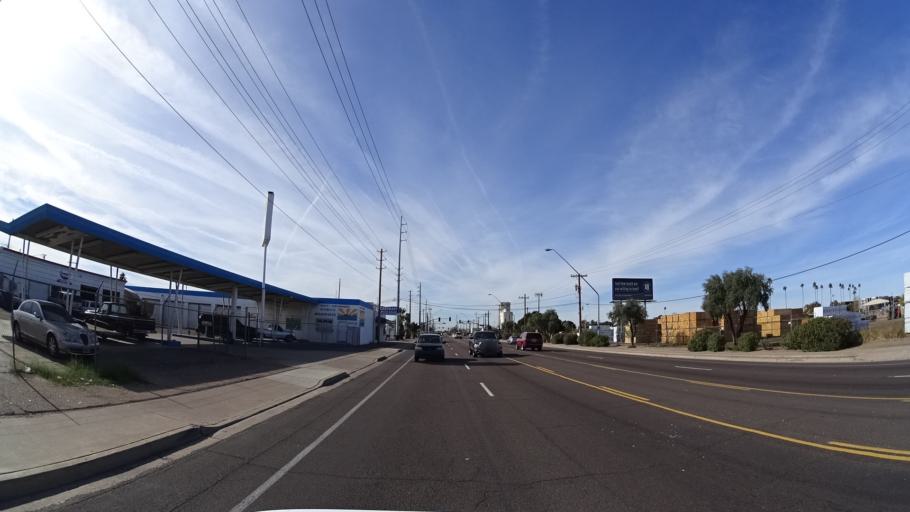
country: US
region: Arizona
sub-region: Maricopa County
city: Mesa
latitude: 33.4077
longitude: -111.8304
